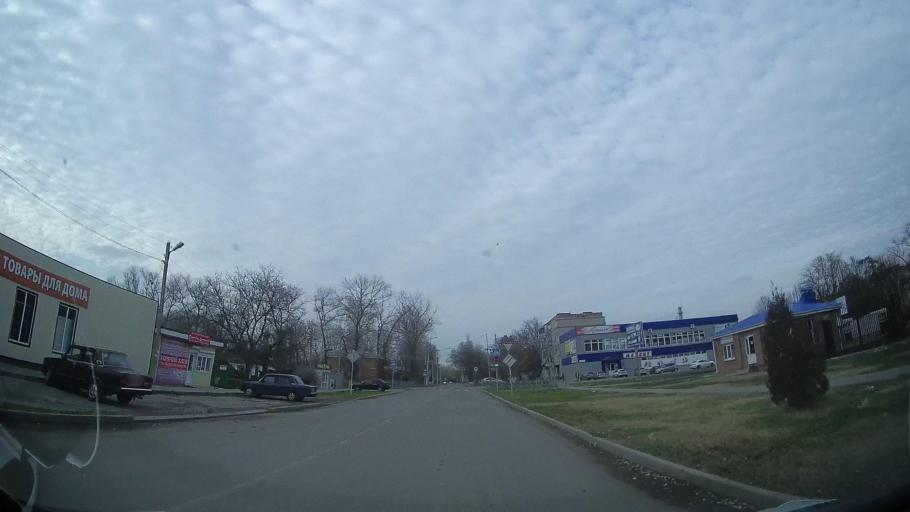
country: RU
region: Rostov
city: Zernograd
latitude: 46.8528
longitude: 40.3134
